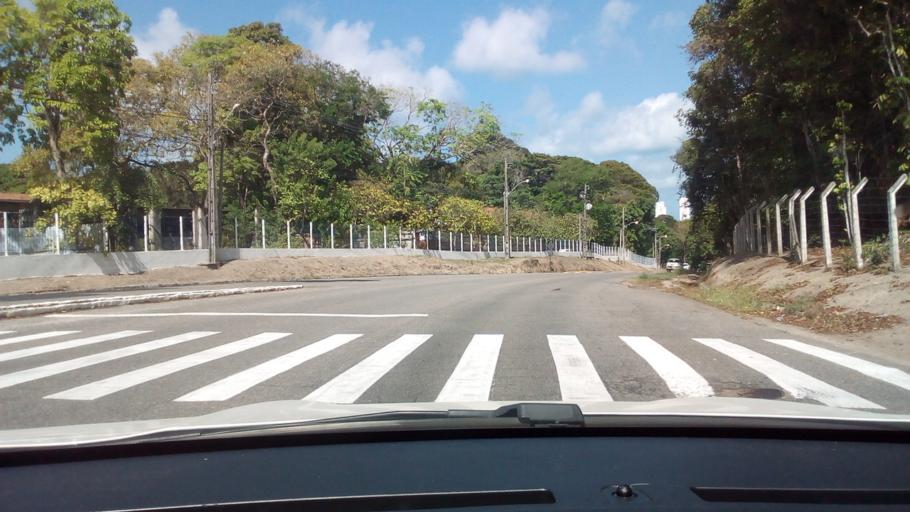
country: BR
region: Paraiba
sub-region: Joao Pessoa
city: Joao Pessoa
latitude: -7.1406
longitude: -34.8452
